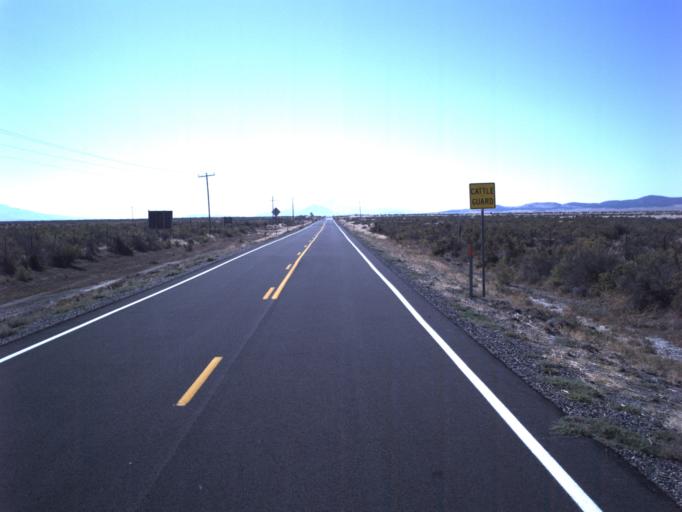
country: US
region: Utah
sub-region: Tooele County
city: Grantsville
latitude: 40.3483
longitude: -112.7453
